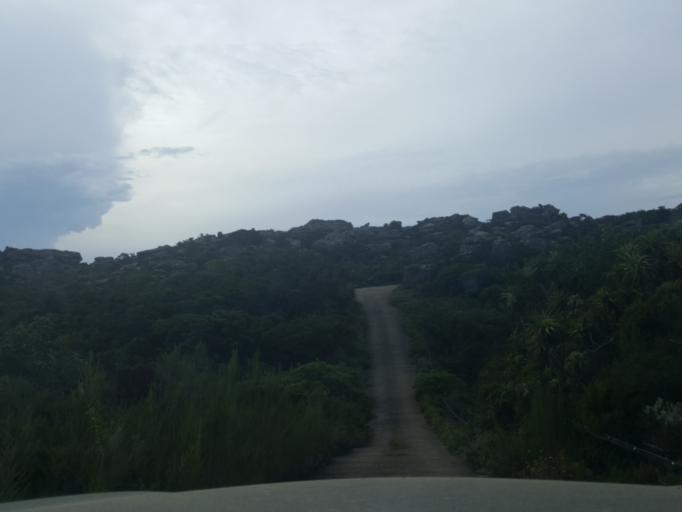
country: ZA
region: Limpopo
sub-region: Mopani District Municipality
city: Hoedspruit
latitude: -24.5531
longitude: 30.8701
